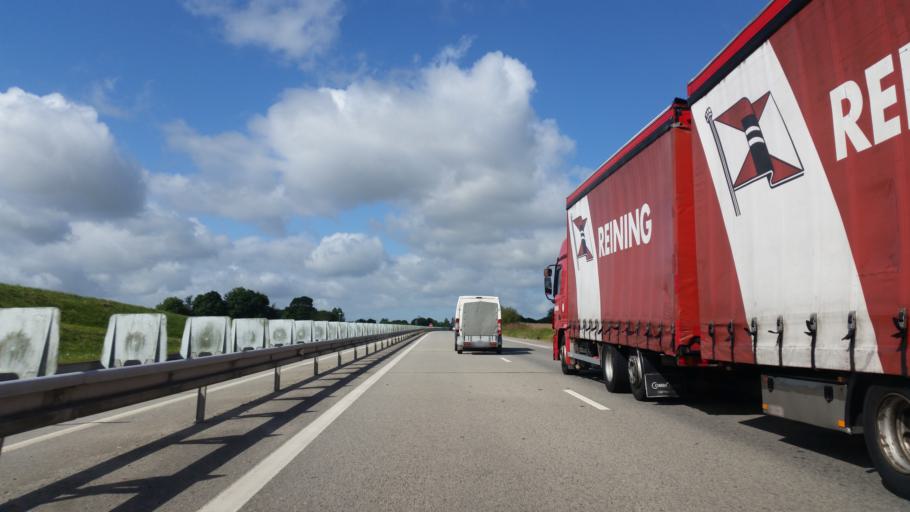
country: FR
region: Lower Normandy
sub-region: Departement du Calvados
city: Isigny-sur-Mer
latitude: 49.3047
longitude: -1.1515
